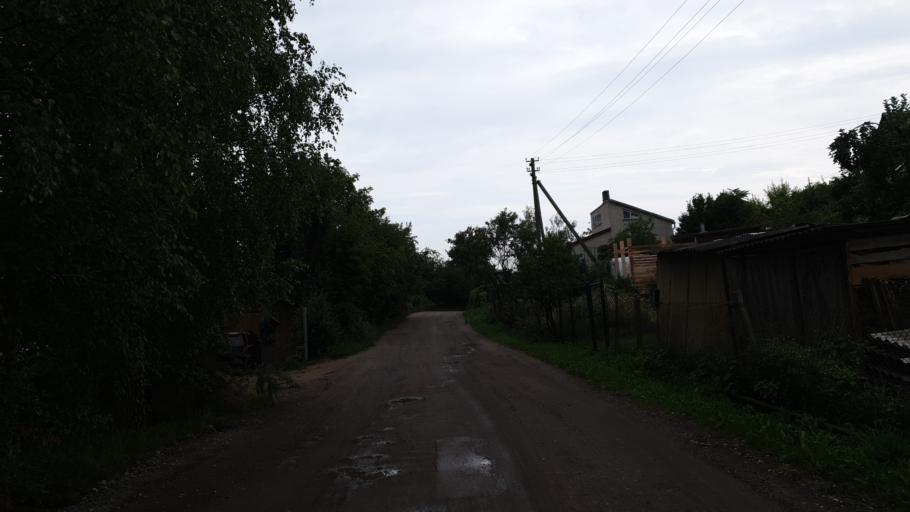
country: LT
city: Grigiskes
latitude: 54.7694
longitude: 25.0160
